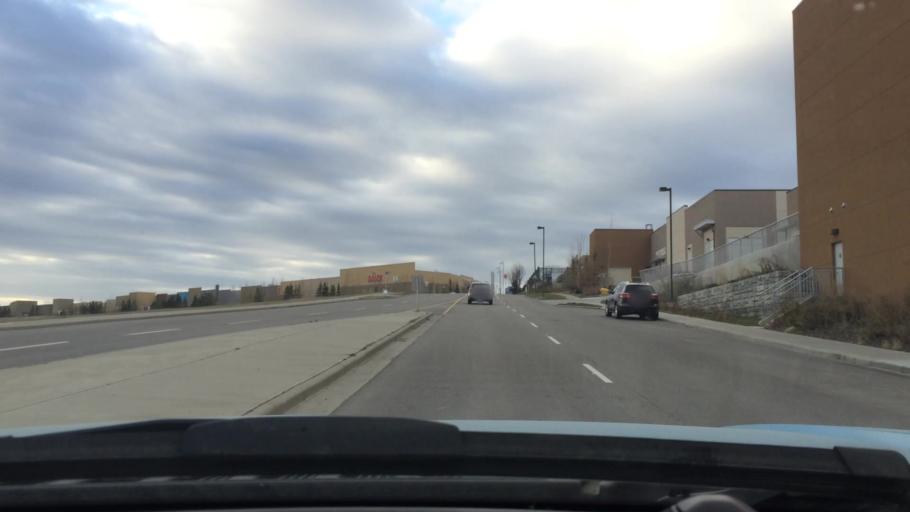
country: CA
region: Alberta
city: Calgary
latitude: 51.1615
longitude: -114.1597
